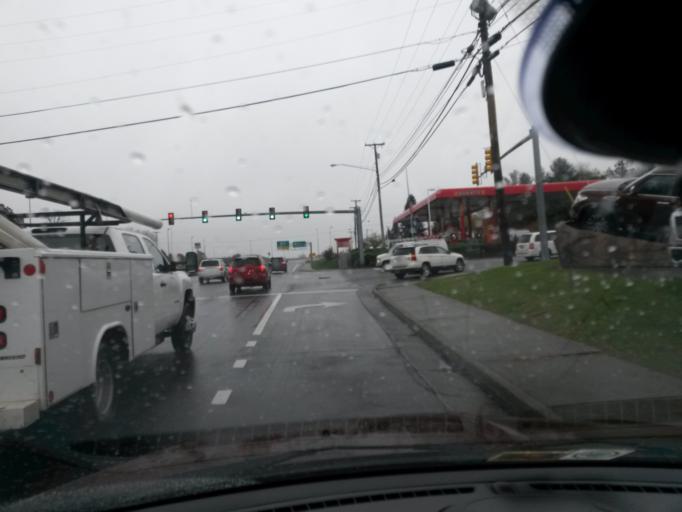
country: US
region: Virginia
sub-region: Montgomery County
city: Christiansburg
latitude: 37.1581
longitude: -80.4190
